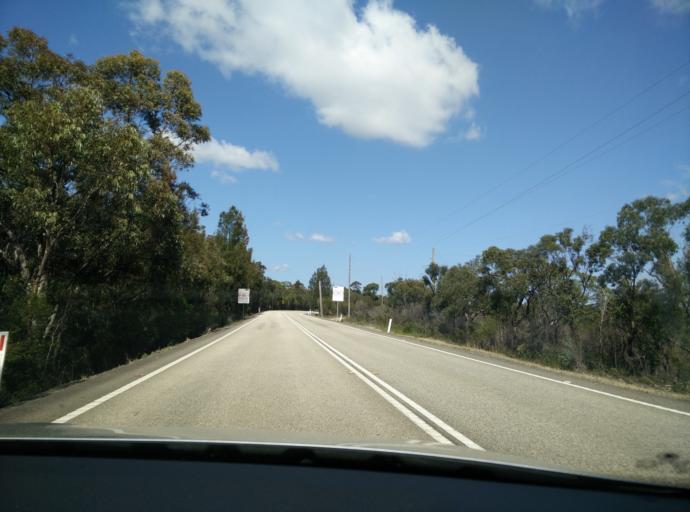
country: AU
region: New South Wales
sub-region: Gosford Shire
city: Point Clare
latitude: -33.4573
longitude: 151.2850
